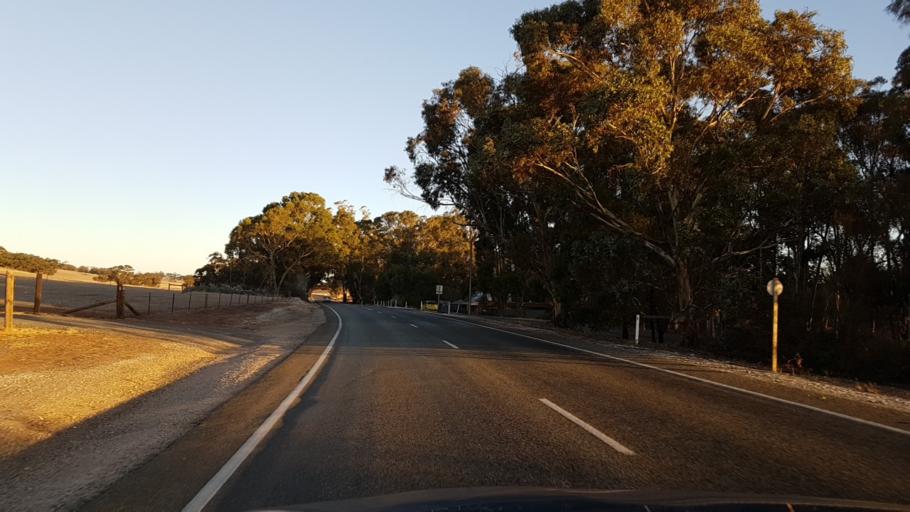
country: AU
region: South Australia
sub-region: Wakefield
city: Balaklava
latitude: -34.1501
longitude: 138.6907
